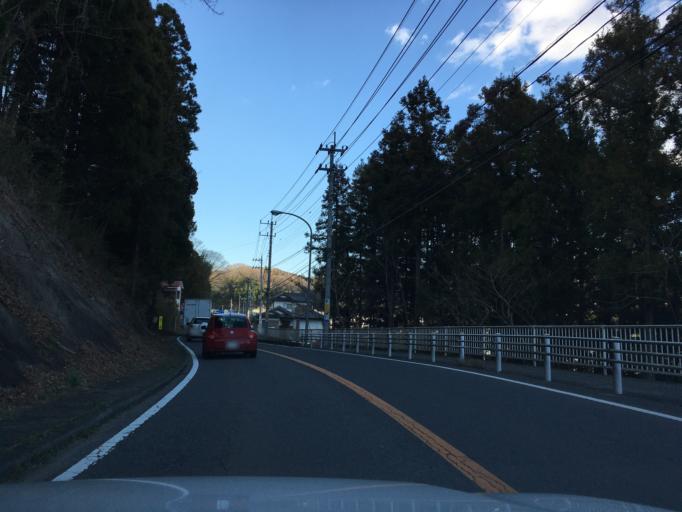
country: JP
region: Ibaraki
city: Daigo
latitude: 36.7550
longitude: 140.3830
